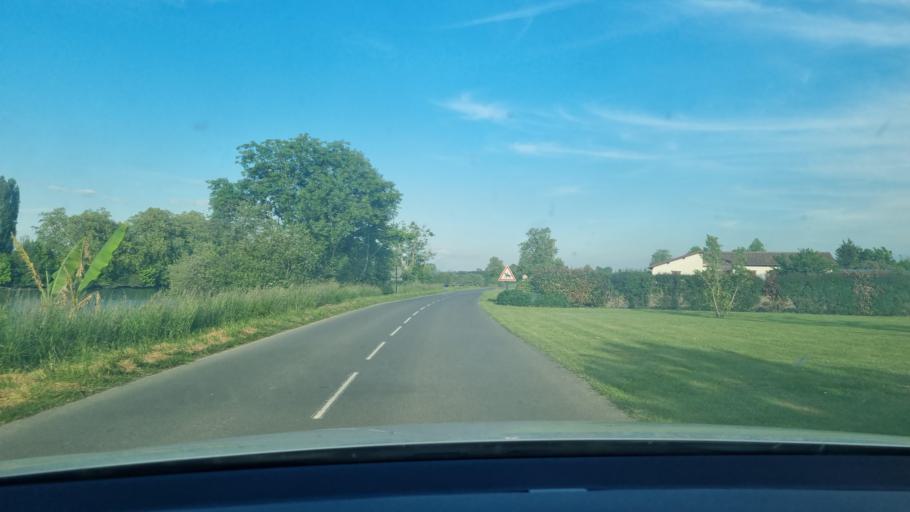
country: FR
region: Aquitaine
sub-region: Departement des Landes
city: Peyrehorade
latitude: 43.5450
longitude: -1.1715
